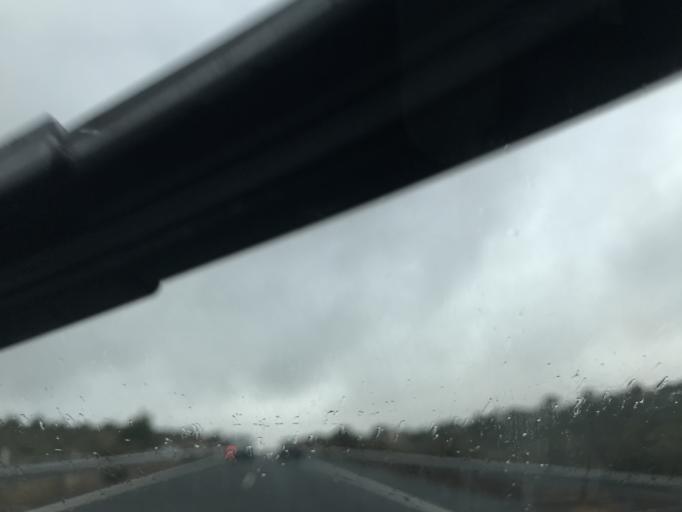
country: ES
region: Andalusia
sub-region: Provincia de Malaga
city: Mollina
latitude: 37.1050
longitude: -4.6512
